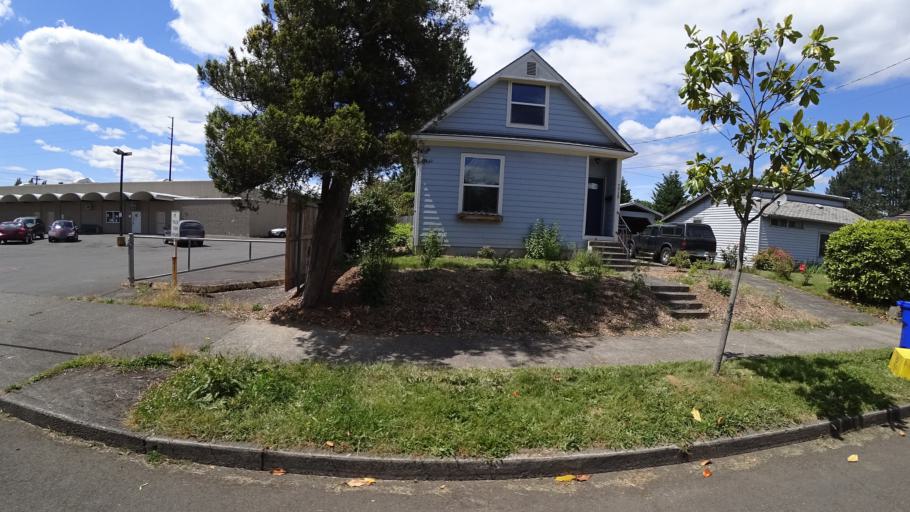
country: US
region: Oregon
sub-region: Multnomah County
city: Portland
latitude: 45.5836
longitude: -122.7241
